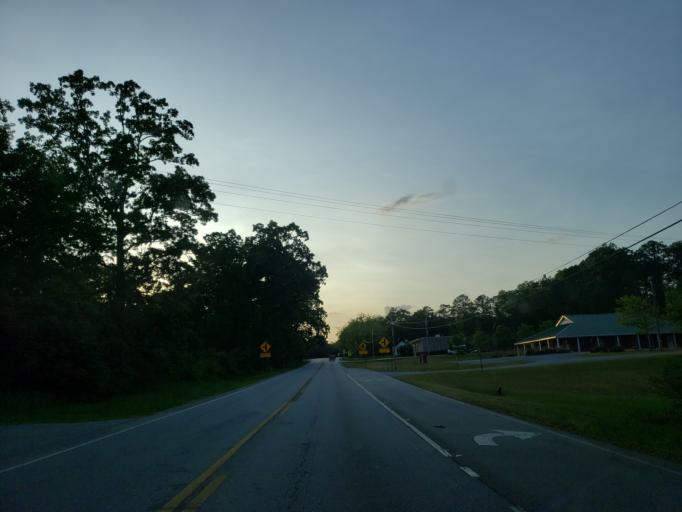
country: US
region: Georgia
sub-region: Coweta County
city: Newnan
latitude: 33.4338
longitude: -84.8692
